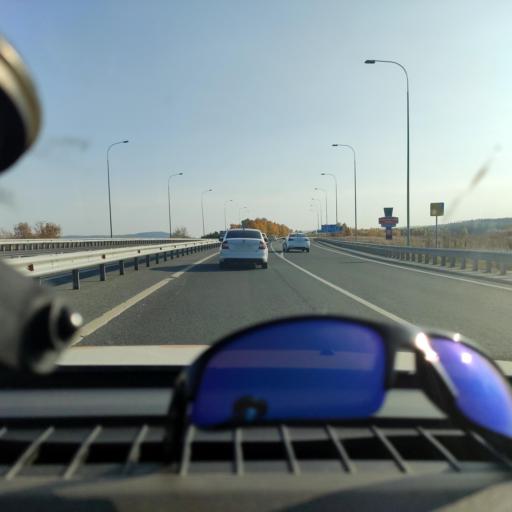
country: RU
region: Samara
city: Bereza
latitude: 53.4953
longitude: 50.1176
